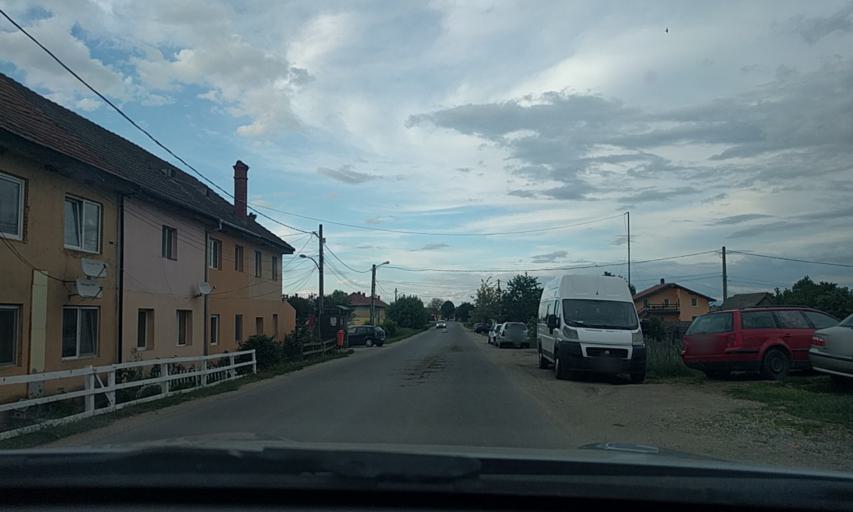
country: RO
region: Brasov
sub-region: Comuna Harman
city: Harman
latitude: 45.7551
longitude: 25.7147
